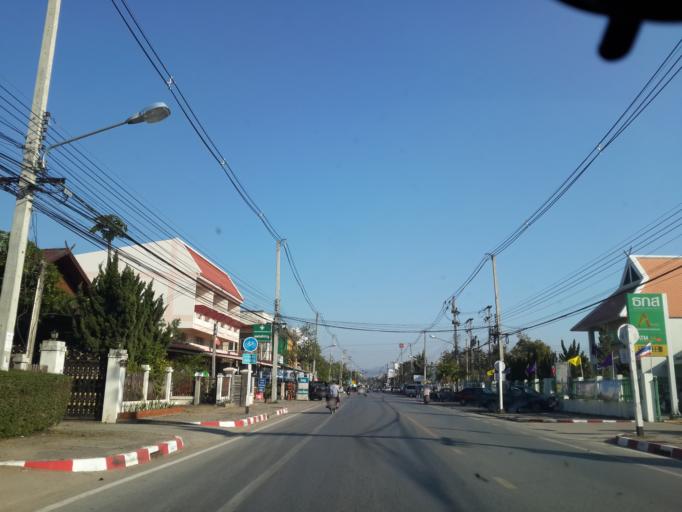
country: TH
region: Chiang Mai
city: San Kamphaeng
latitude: 18.7473
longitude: 99.1155
